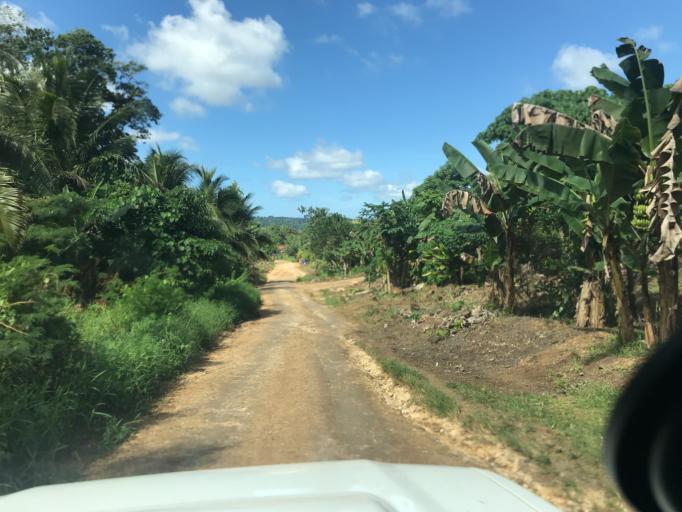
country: VU
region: Sanma
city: Luganville
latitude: -15.5292
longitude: 167.1501
